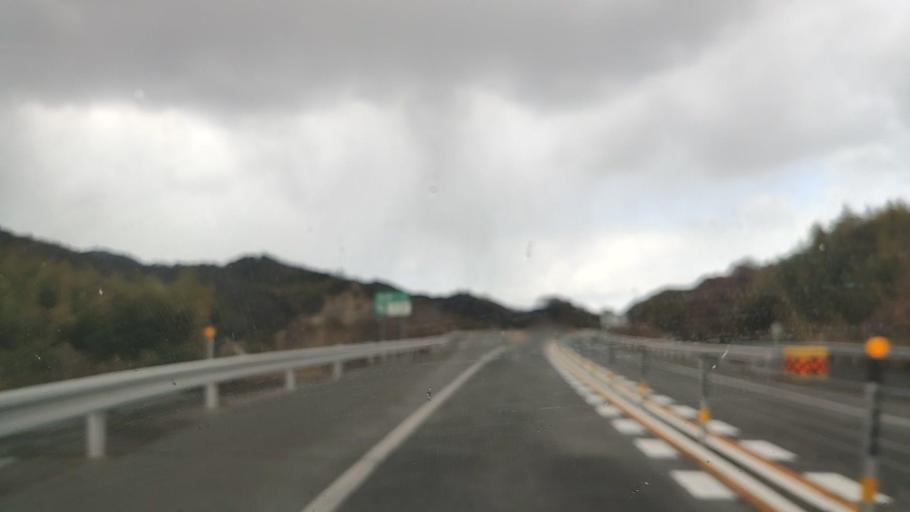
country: JP
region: Hiroshima
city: Innoshima
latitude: 34.1541
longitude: 133.0653
